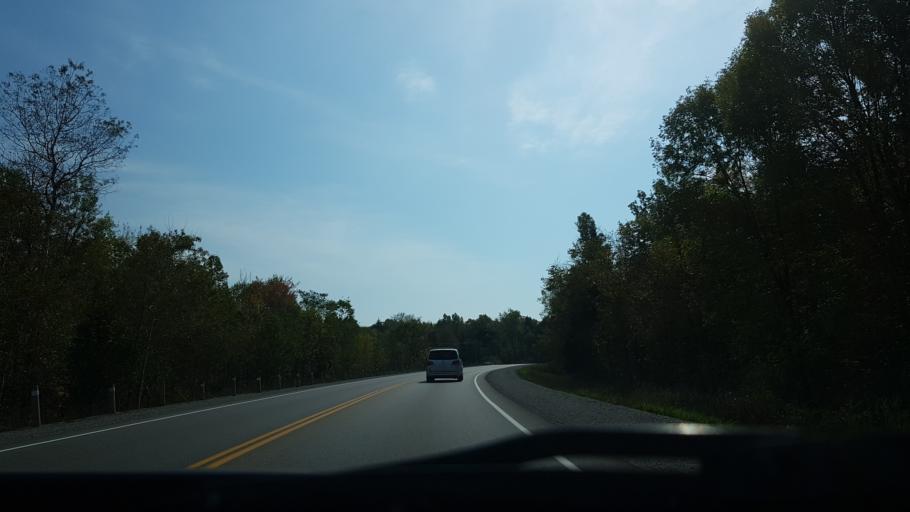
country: CA
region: Ontario
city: Orillia
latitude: 44.7394
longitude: -79.2937
